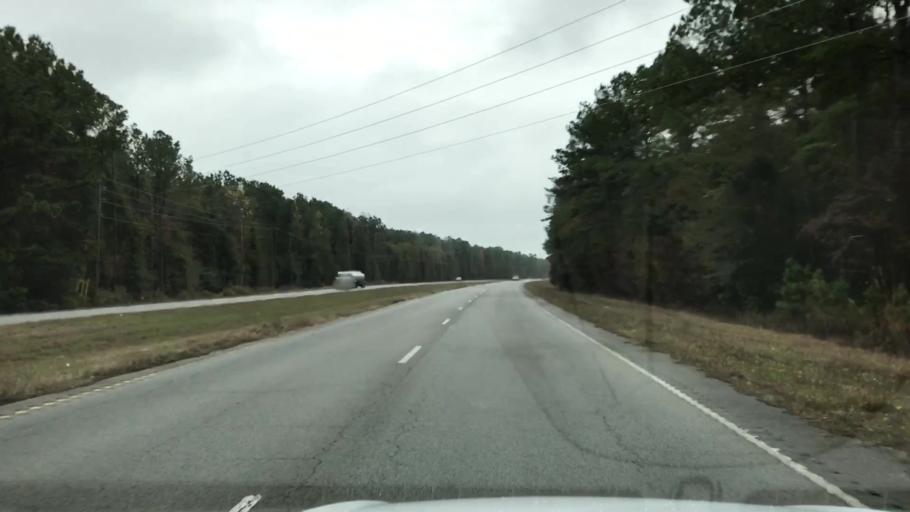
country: US
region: South Carolina
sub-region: Charleston County
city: Awendaw
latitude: 32.9538
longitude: -79.6942
